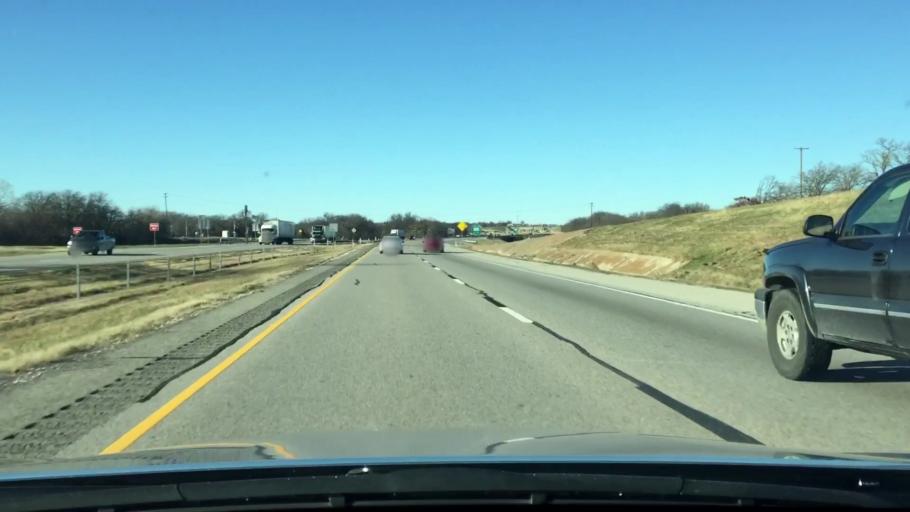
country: US
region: Texas
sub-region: Johnson County
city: Grandview
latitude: 32.2874
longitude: -97.1777
